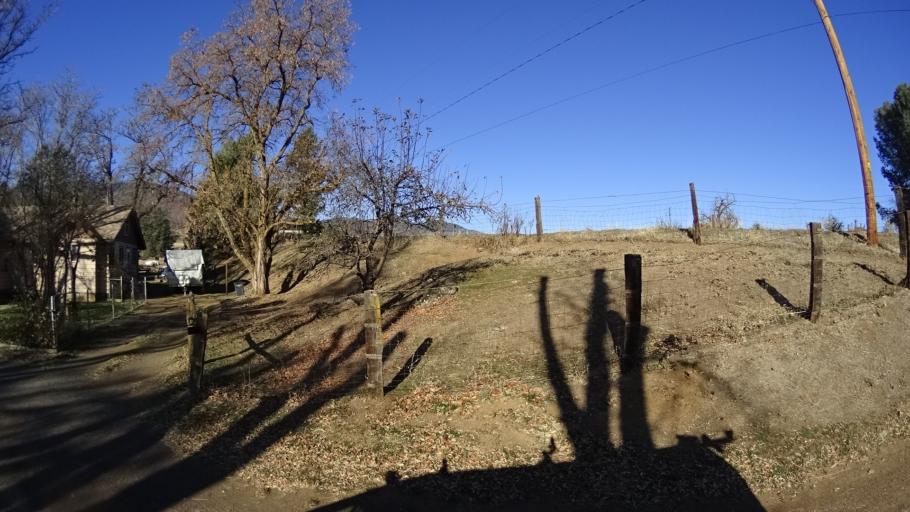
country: US
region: California
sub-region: Siskiyou County
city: Montague
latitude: 41.9096
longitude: -122.5630
